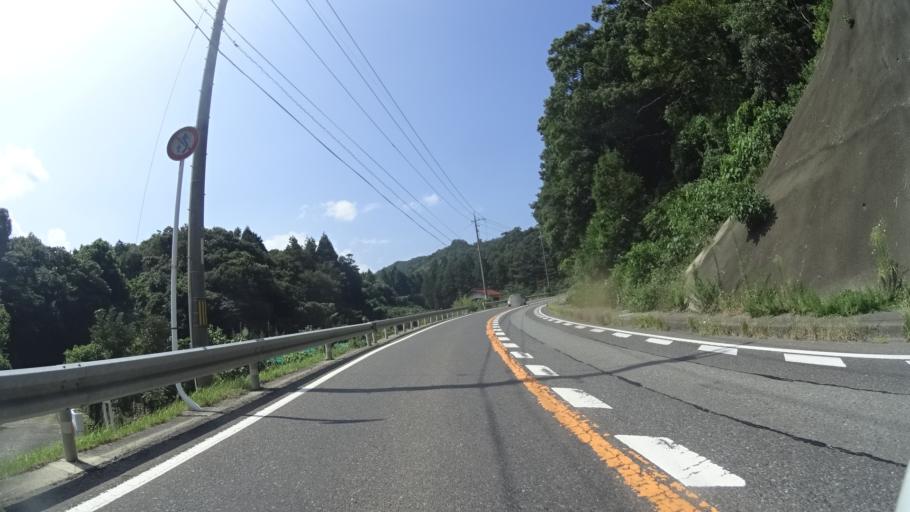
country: JP
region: Shimane
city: Masuda
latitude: 34.6672
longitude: 131.6999
